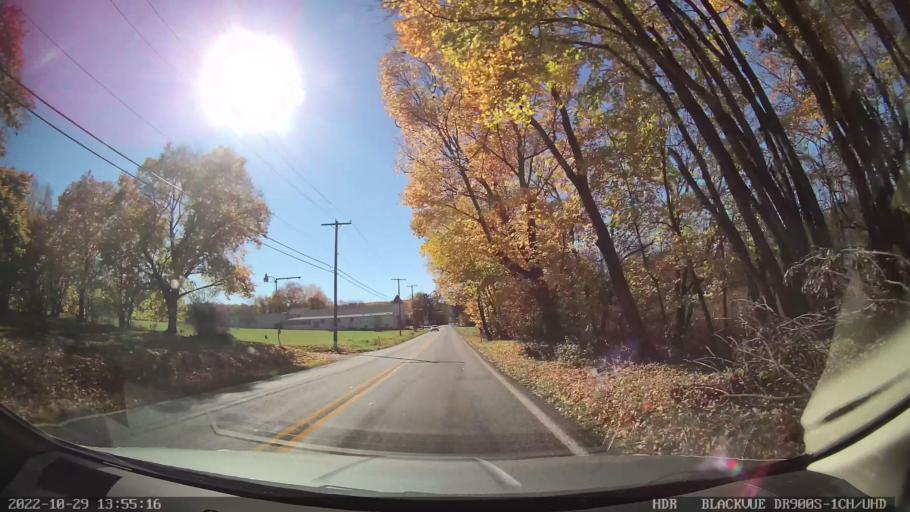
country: US
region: Pennsylvania
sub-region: Lehigh County
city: Emmaus
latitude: 40.5073
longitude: -75.4941
